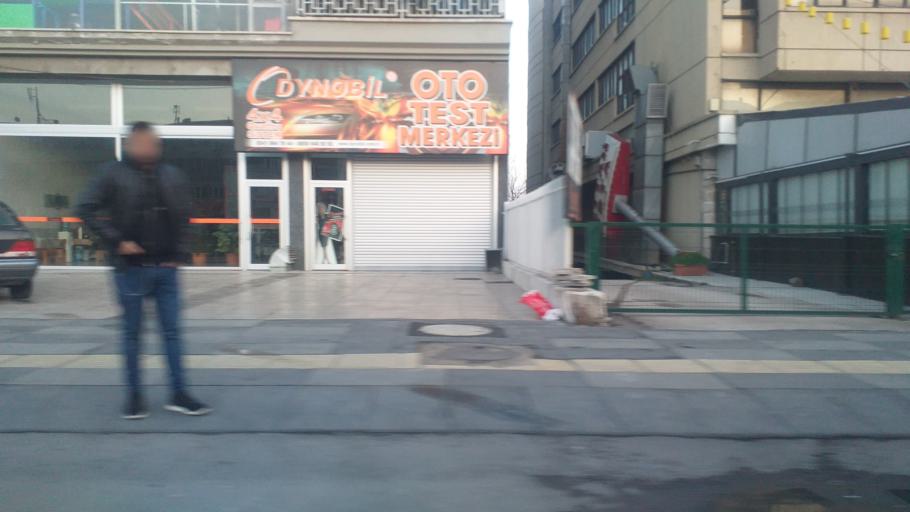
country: TR
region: Ankara
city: Ankara
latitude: 39.9508
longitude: 32.8534
